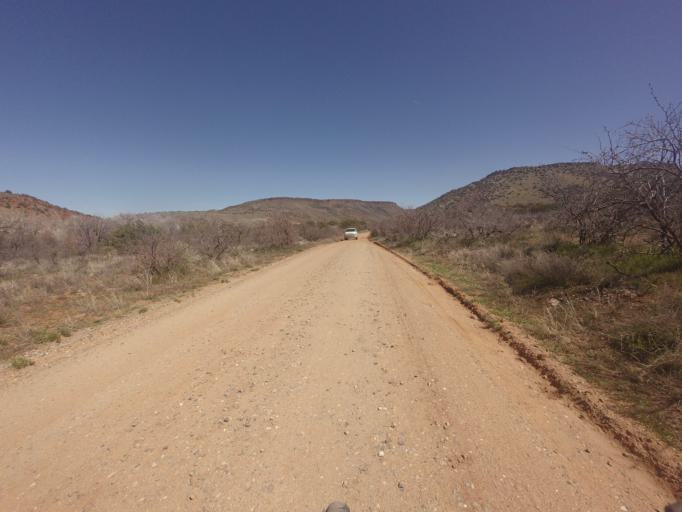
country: US
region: Arizona
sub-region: Yavapai County
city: Lake Montezuma
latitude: 34.6661
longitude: -111.7156
